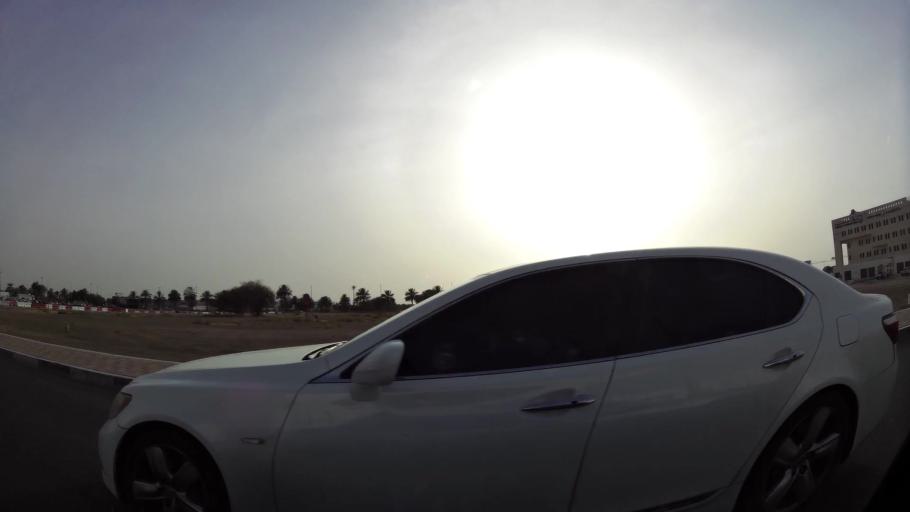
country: AE
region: Abu Dhabi
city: Al Ain
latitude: 24.2392
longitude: 55.7305
